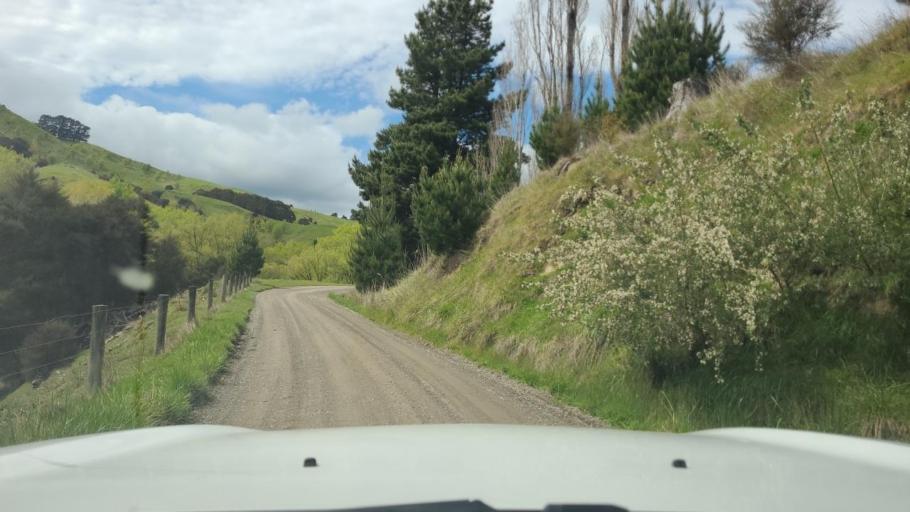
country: NZ
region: Wellington
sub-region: South Wairarapa District
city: Waipawa
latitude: -41.2772
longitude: 175.5524
